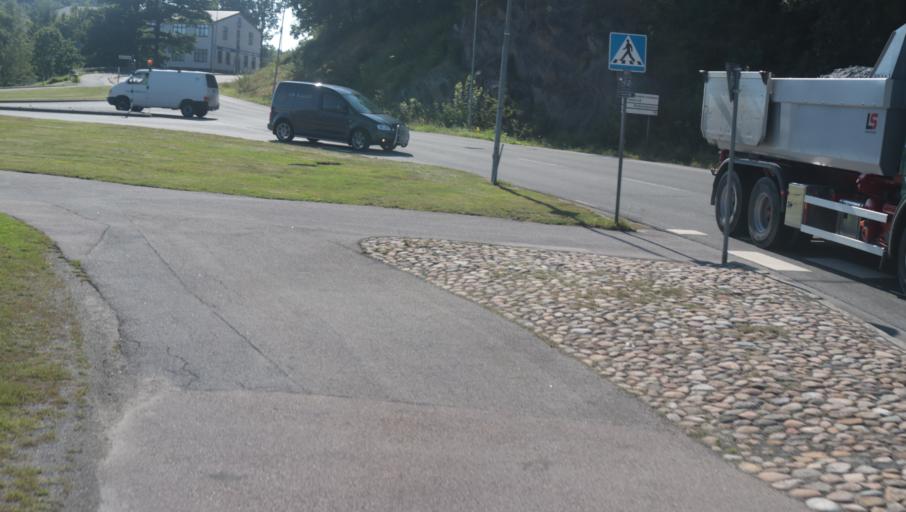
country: SE
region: Blekinge
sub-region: Karlshamns Kommun
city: Karlshamn
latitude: 56.1806
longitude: 14.8484
